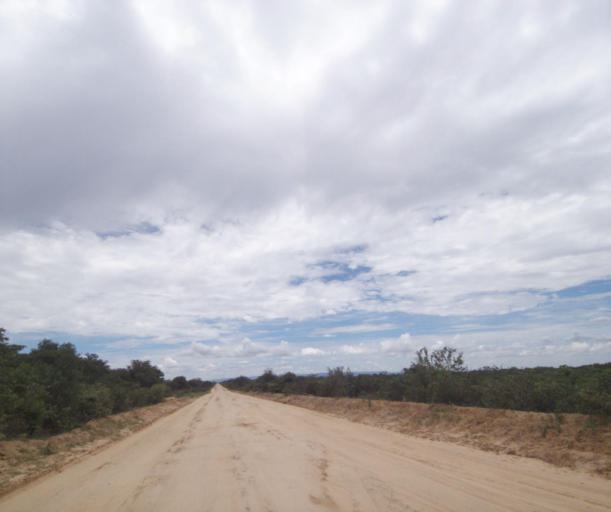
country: BR
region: Bahia
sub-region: Carinhanha
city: Carinhanha
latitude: -14.2703
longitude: -43.8081
